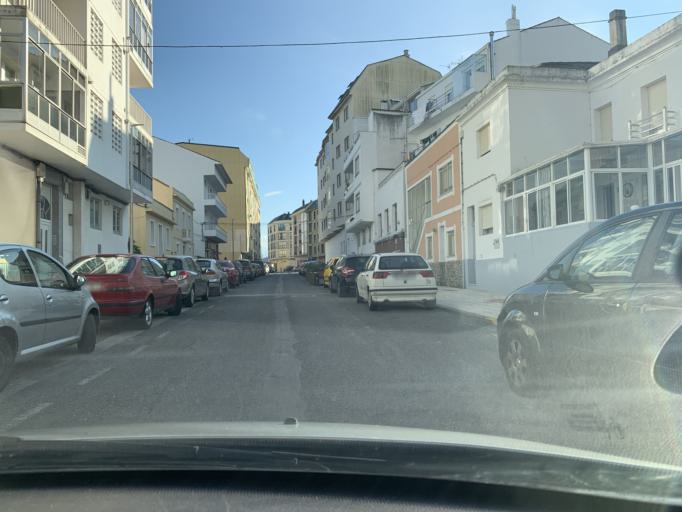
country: ES
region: Galicia
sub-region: Provincia de Lugo
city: Foz
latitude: 43.5726
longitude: -7.2517
